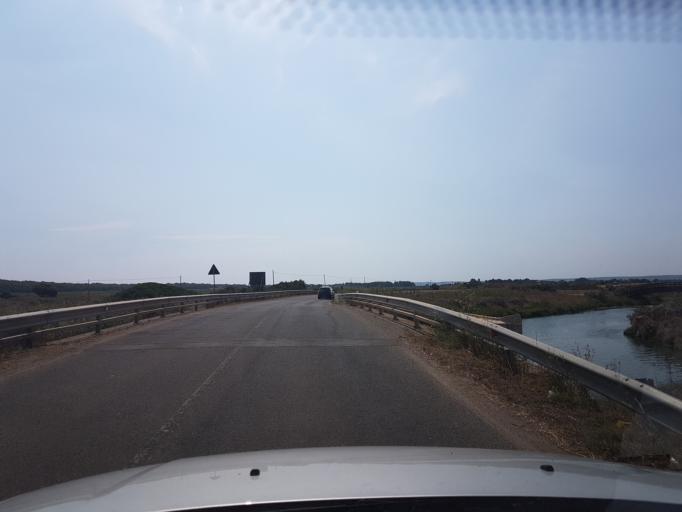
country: IT
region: Sardinia
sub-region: Provincia di Oristano
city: Cabras
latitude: 39.9182
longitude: 8.5190
